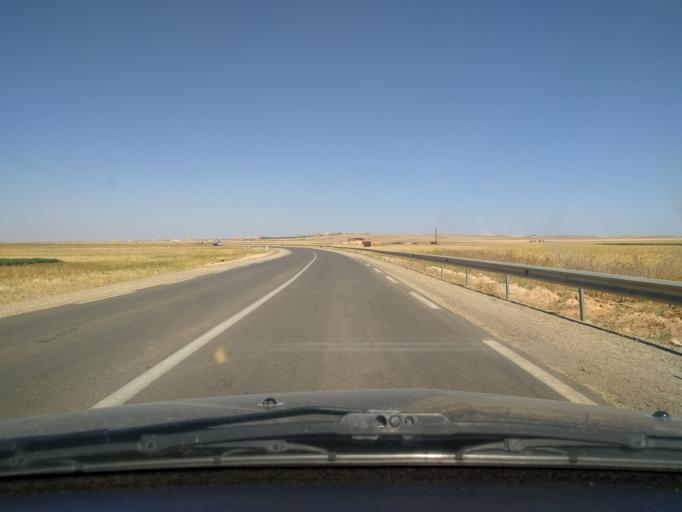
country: DZ
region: Tiaret
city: Frenda
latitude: 34.9045
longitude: 1.1467
